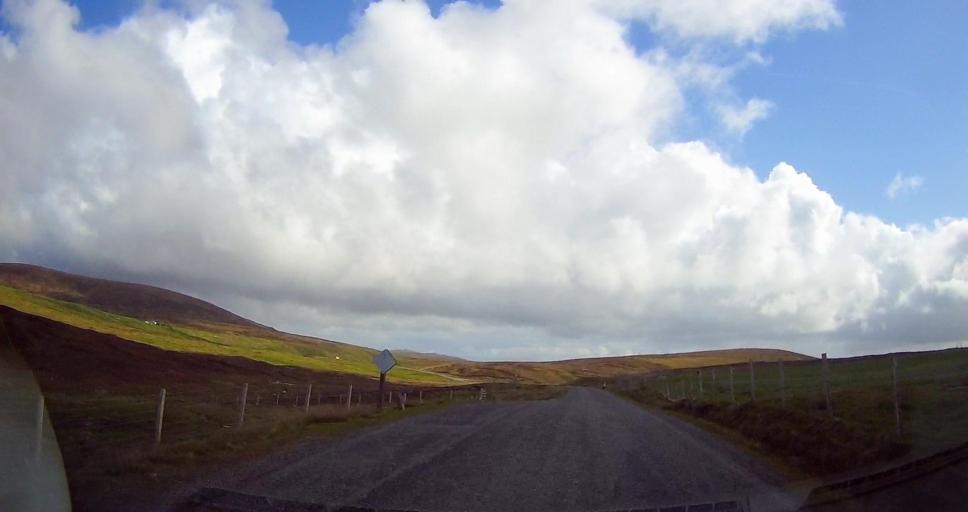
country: GB
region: Scotland
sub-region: Shetland Islands
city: Lerwick
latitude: 60.5137
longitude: -1.3828
